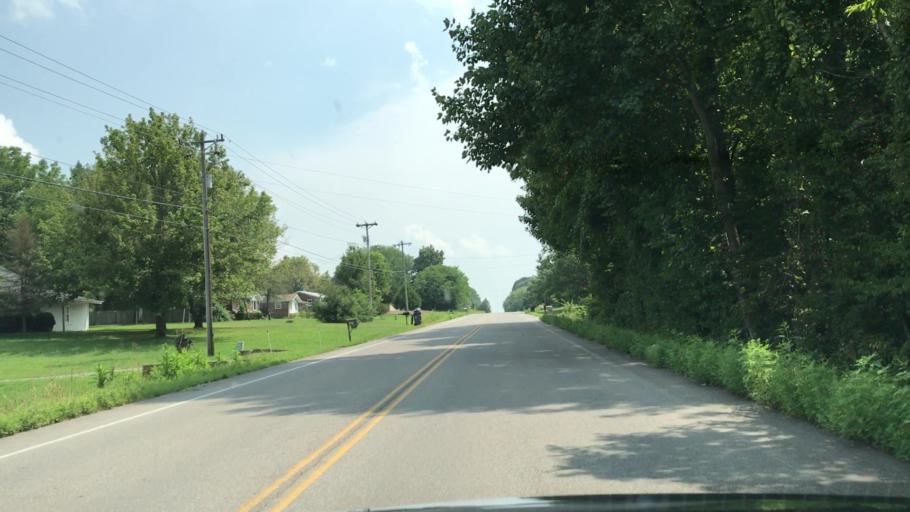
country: US
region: Tennessee
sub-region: Sumner County
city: Portland
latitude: 36.5200
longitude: -86.5013
